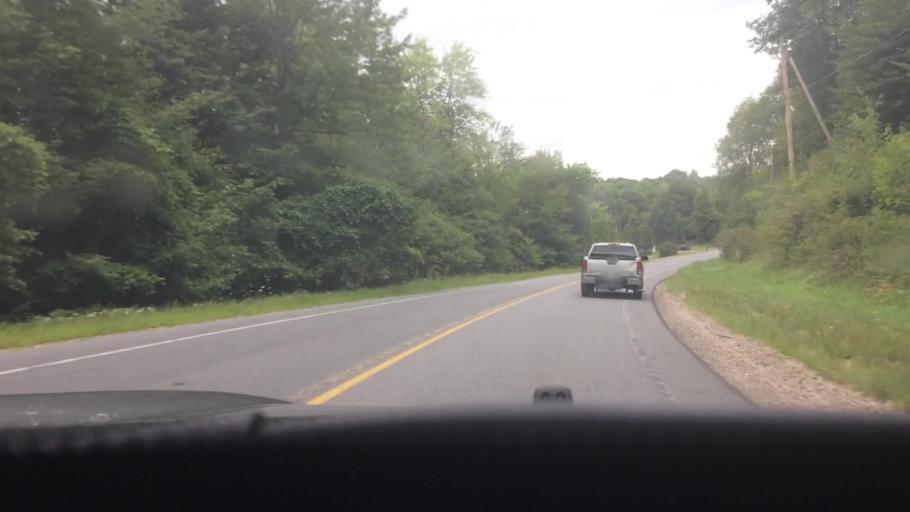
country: US
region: New York
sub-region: St. Lawrence County
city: Canton
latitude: 44.5211
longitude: -75.1957
